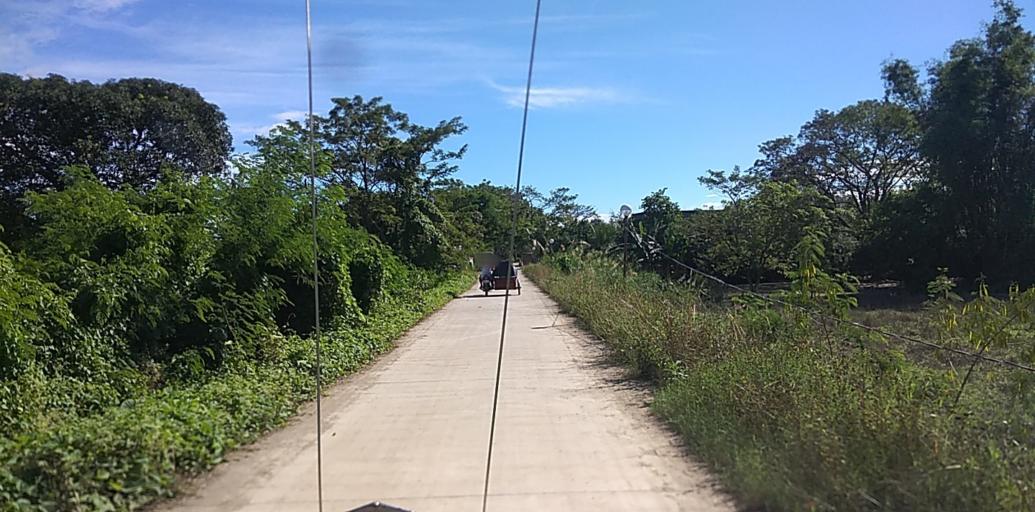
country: PH
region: Central Luzon
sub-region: Province of Pampanga
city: San Nicolas
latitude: 15.0646
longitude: 120.8091
